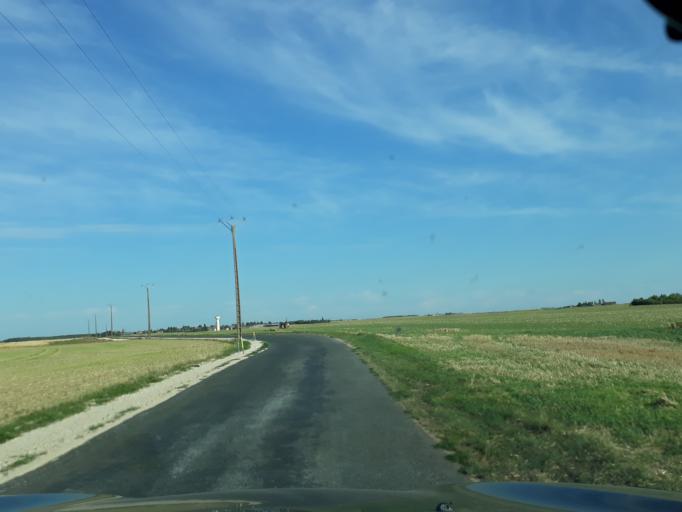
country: FR
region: Centre
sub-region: Departement du Loir-et-Cher
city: Ouzouer-le-Marche
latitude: 47.9362
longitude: 1.5521
